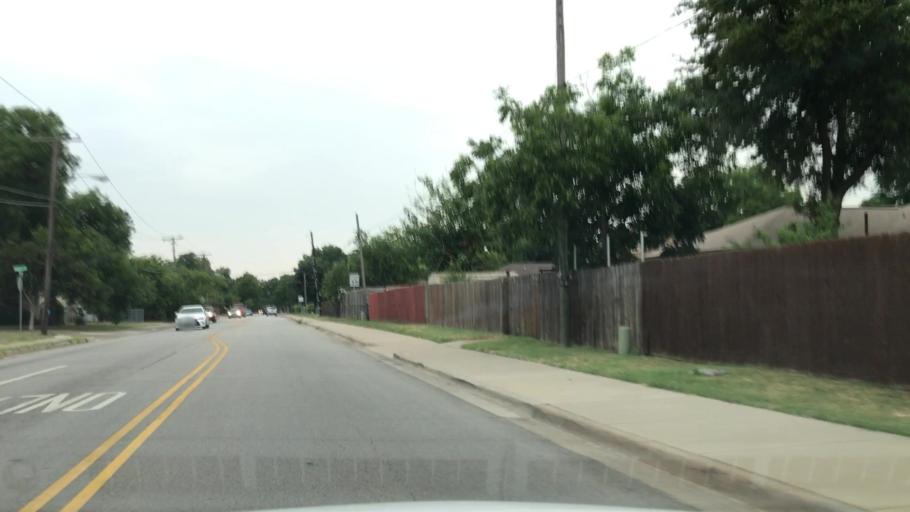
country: US
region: Texas
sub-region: Dallas County
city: Carrollton
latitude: 32.9683
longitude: -96.9073
